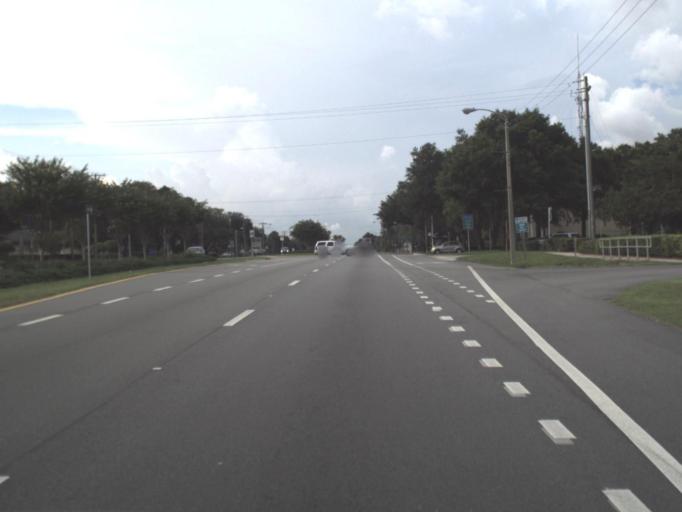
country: US
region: Florida
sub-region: Hillsborough County
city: Temple Terrace
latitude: 28.0518
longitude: -82.3938
